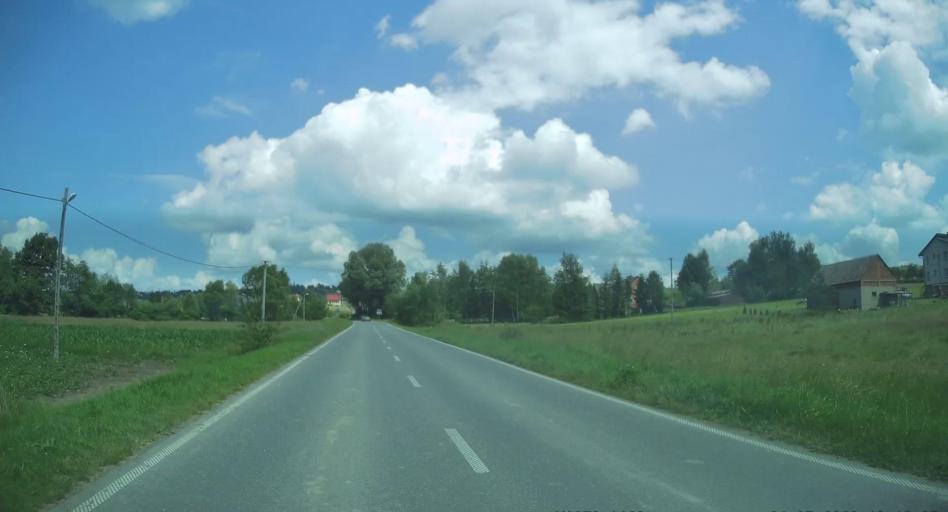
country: PL
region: Lesser Poland Voivodeship
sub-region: Powiat nowosadecki
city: Korzenna
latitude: 49.6760
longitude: 20.7779
